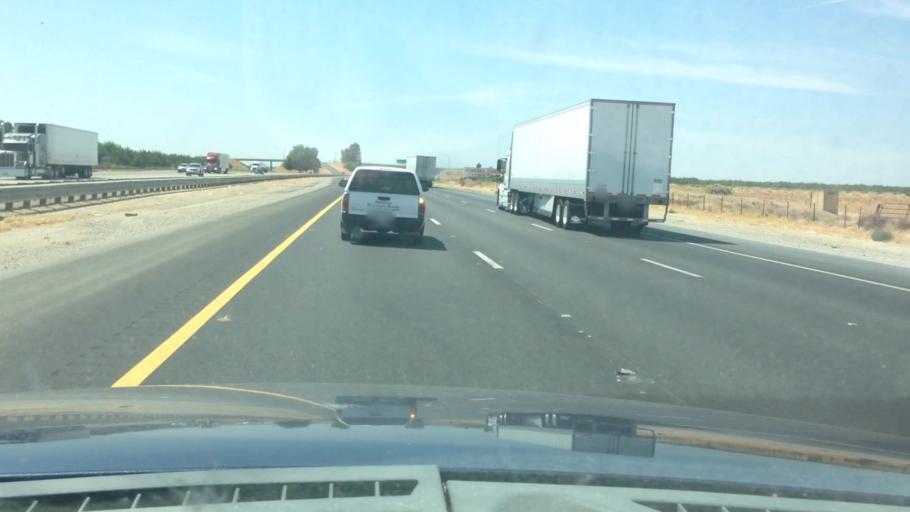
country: US
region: California
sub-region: Kern County
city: McFarland
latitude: 35.6530
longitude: -119.2216
